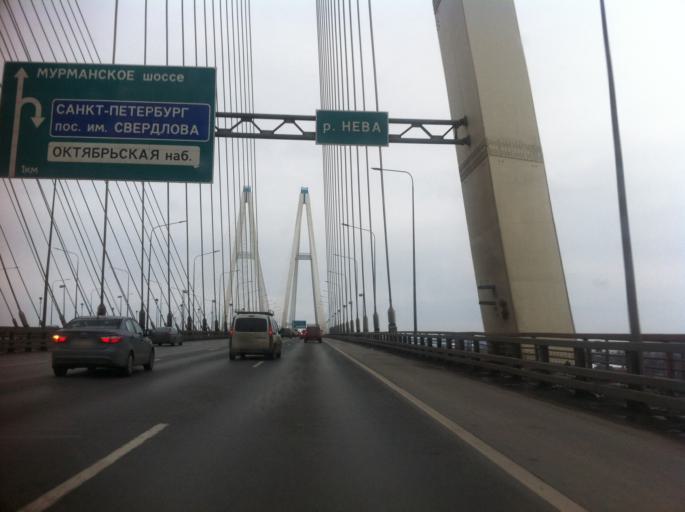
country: RU
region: Leningrad
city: Rybatskoye
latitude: 59.8534
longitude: 30.4863
